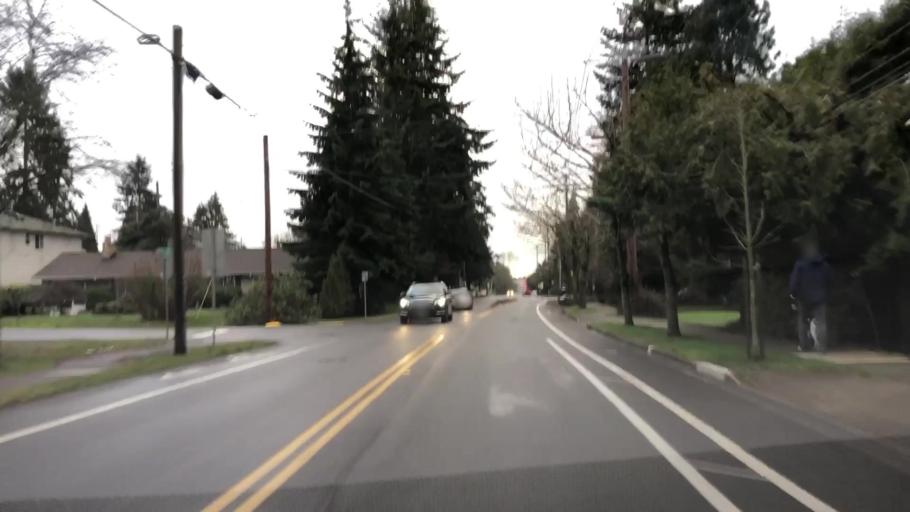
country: US
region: Washington
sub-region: King County
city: Kirkland
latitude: 47.6753
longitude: -122.1744
